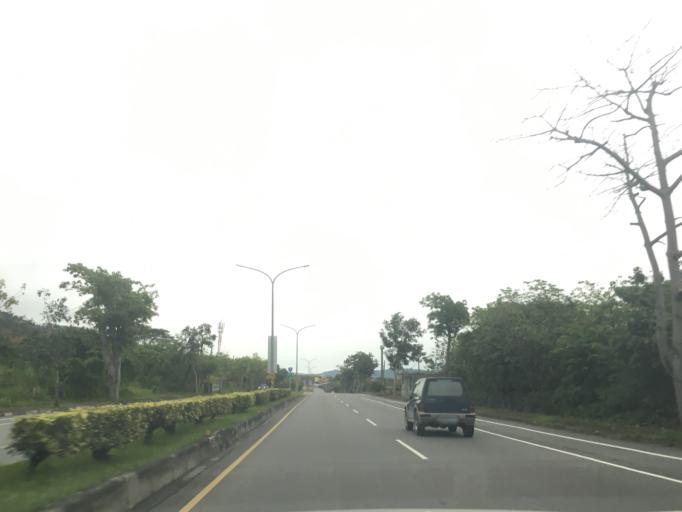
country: TW
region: Taiwan
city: Taitung City
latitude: 22.7211
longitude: 121.0539
